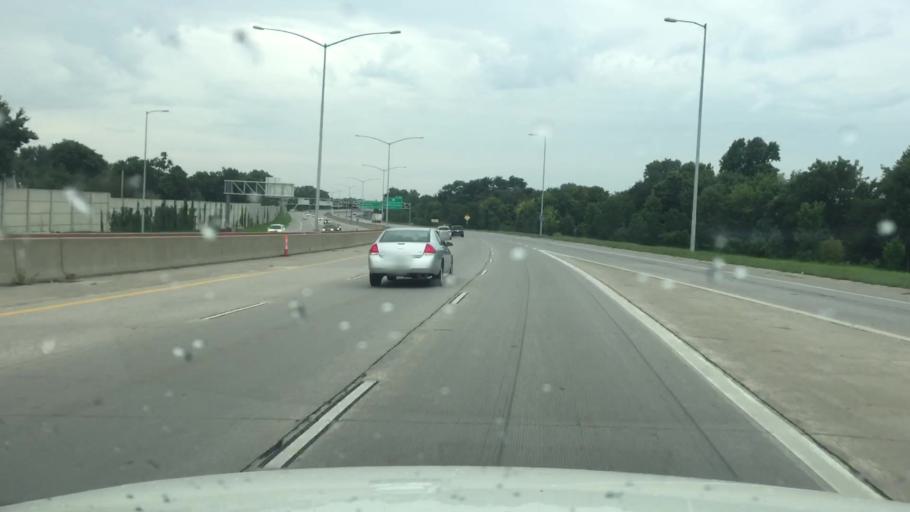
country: US
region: Iowa
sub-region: Polk County
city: Des Moines
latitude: 41.6125
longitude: -93.5787
